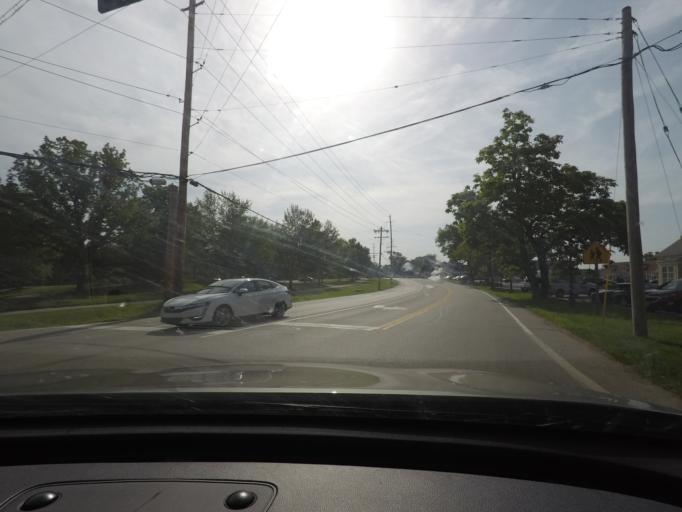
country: US
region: Missouri
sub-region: Saint Louis County
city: Town and Country
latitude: 38.6274
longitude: -90.4830
